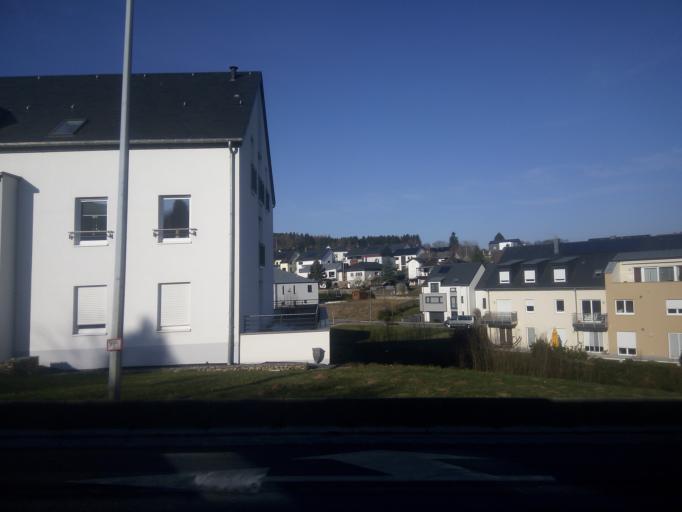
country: LU
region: Grevenmacher
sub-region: Canton de Grevenmacher
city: Junglinster
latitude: 49.7064
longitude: 6.2492
